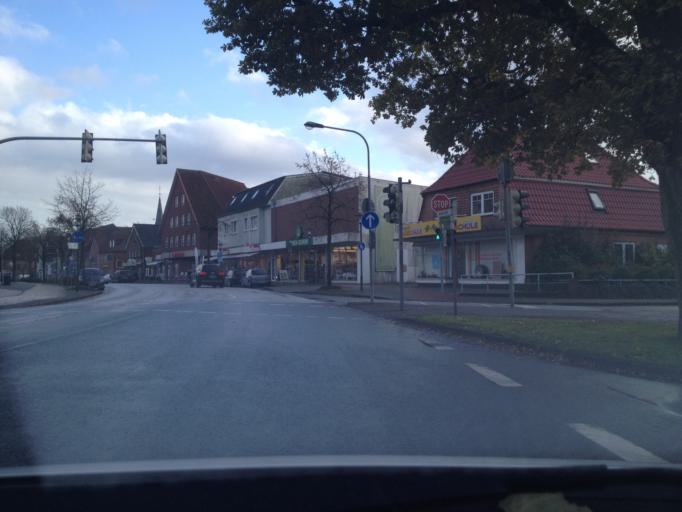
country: DE
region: Schleswig-Holstein
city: Leck
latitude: 54.7736
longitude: 8.9690
